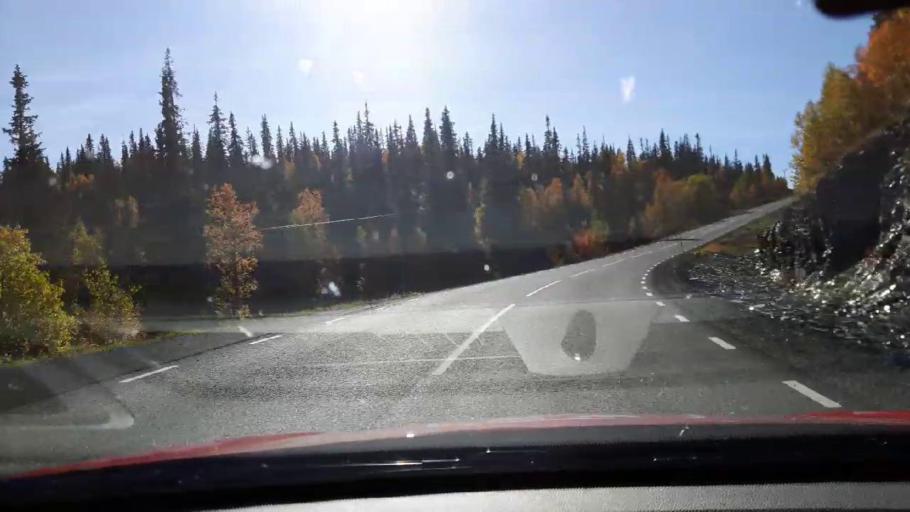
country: NO
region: Nord-Trondelag
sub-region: Royrvik
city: Royrvik
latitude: 64.8495
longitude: 14.1776
